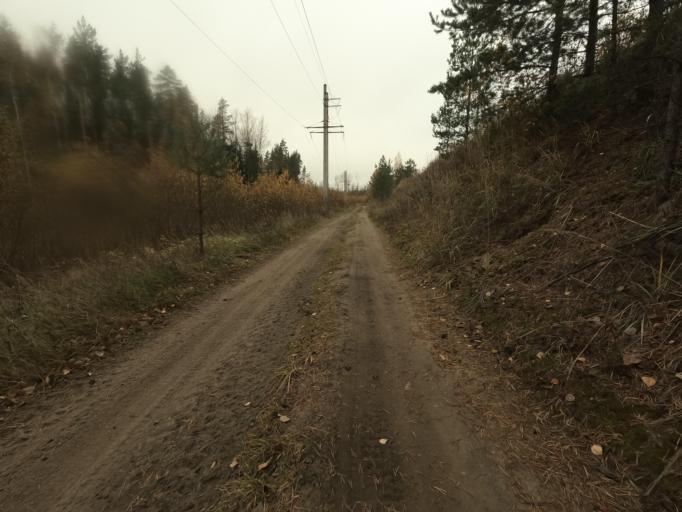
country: RU
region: Leningrad
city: Pavlovo
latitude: 59.7700
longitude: 30.9091
